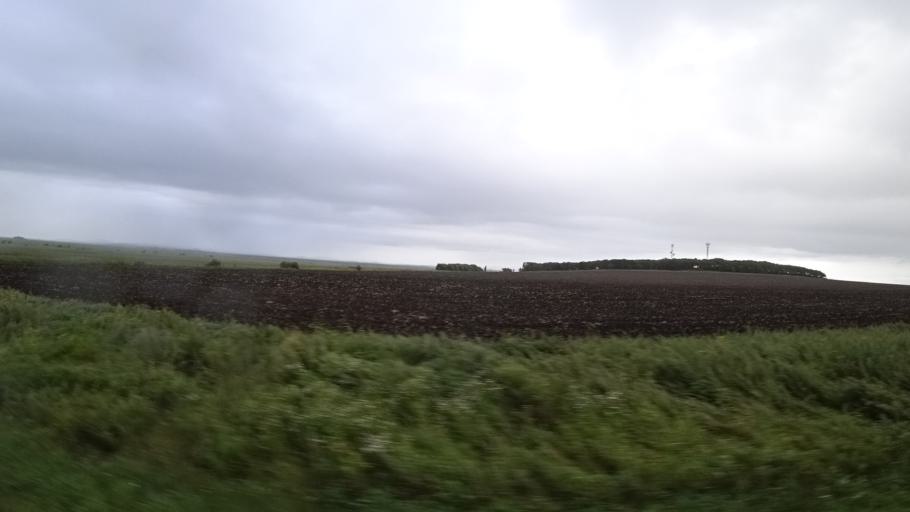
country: RU
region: Primorskiy
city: Chernigovka
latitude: 44.3717
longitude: 132.5300
